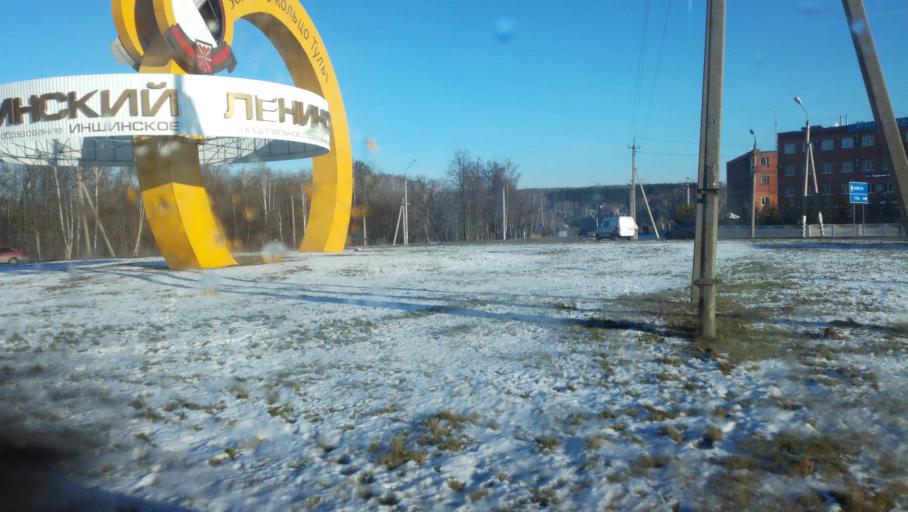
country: RU
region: Tula
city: Kosaya Gora
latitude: 54.1638
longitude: 37.4654
